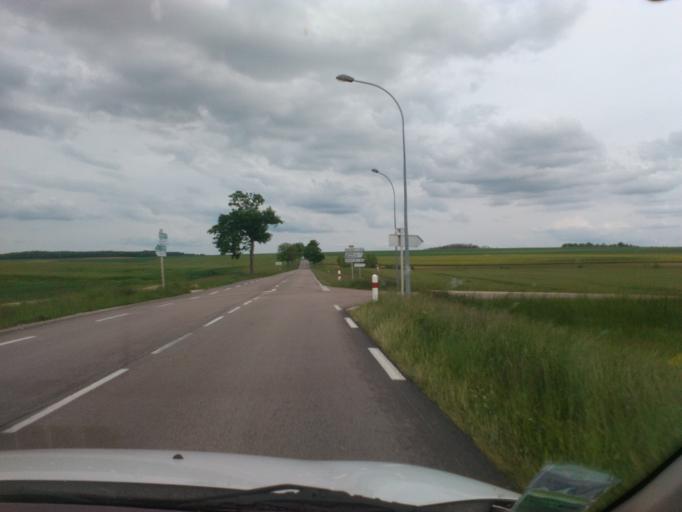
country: FR
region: Champagne-Ardenne
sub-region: Departement de l'Aube
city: Vendeuvre-sur-Barse
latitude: 48.2384
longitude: 4.4860
